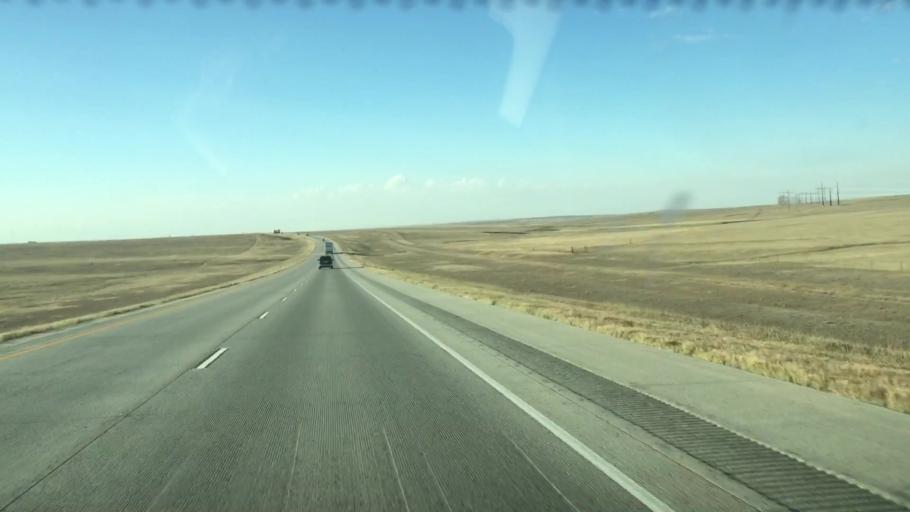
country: US
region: Colorado
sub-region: Lincoln County
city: Limon
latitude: 39.4077
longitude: -103.8981
